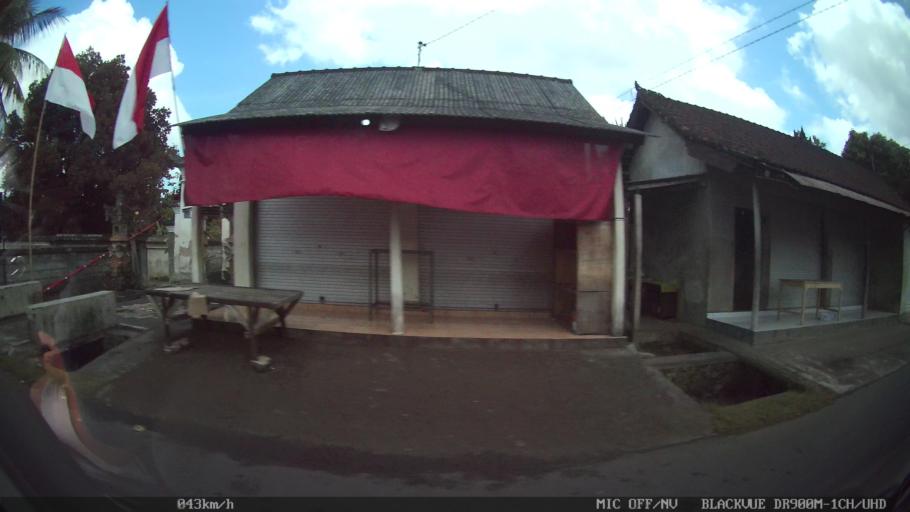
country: ID
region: Bali
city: Banjar Sedang
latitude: -8.5665
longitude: 115.2860
